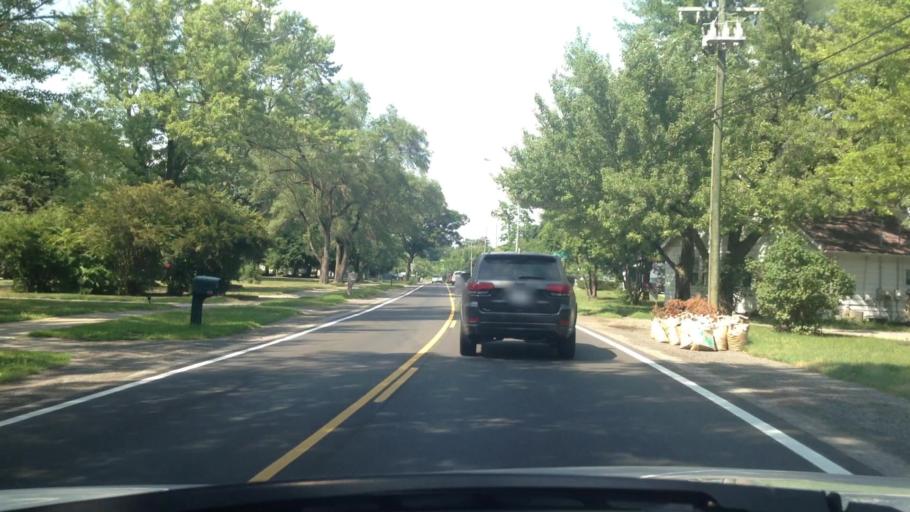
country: US
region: Michigan
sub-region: Oakland County
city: Waterford
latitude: 42.6973
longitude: -83.3711
